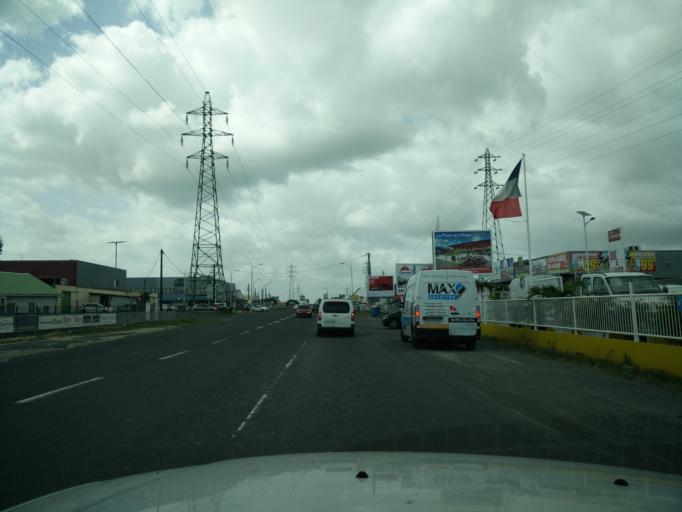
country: GP
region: Guadeloupe
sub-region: Guadeloupe
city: Pointe-a-Pitre
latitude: 16.2413
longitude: -61.5552
